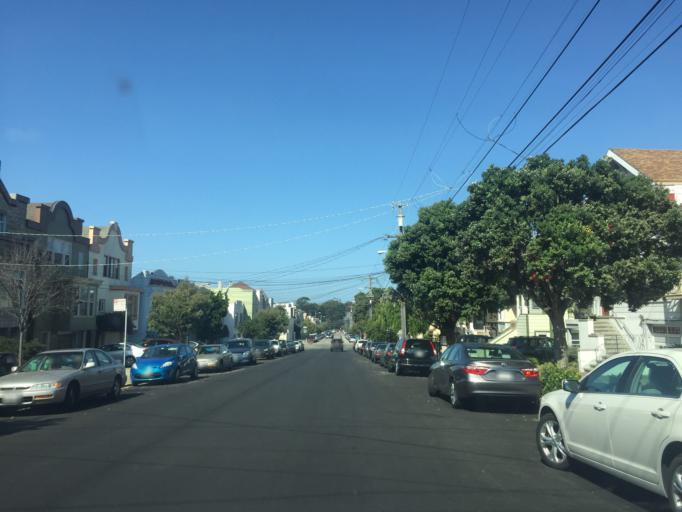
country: US
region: California
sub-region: San Mateo County
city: Daly City
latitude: 37.7603
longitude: -122.4833
